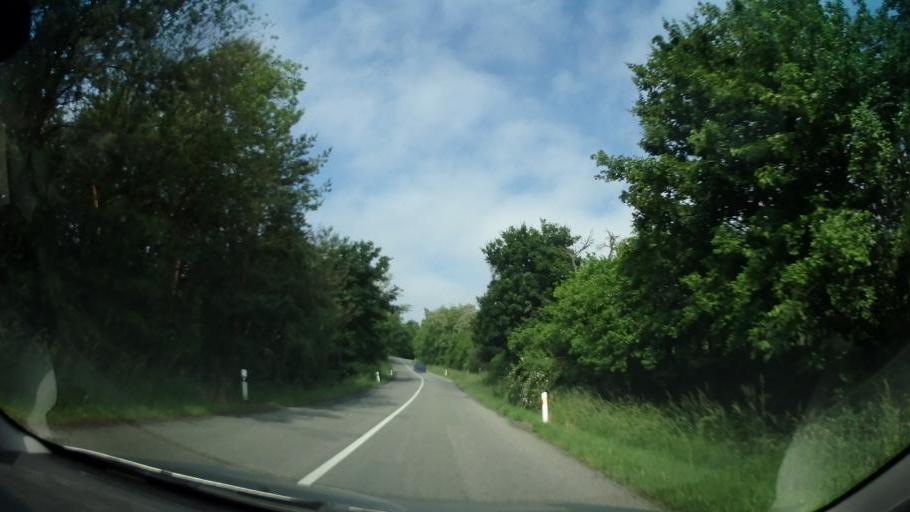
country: CZ
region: South Moravian
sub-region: Okres Brno-Venkov
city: Dolni Loucky
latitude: 49.3705
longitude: 16.3716
